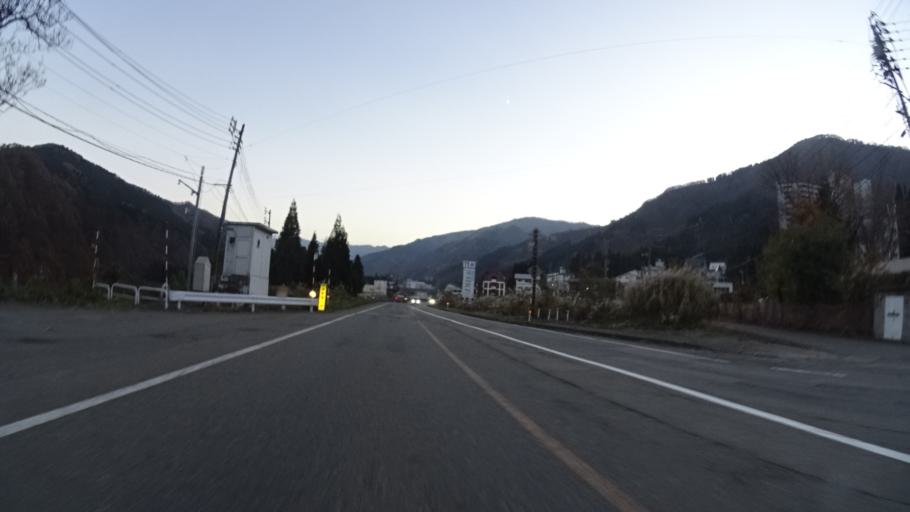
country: JP
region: Niigata
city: Shiozawa
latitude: 36.9666
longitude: 138.8016
